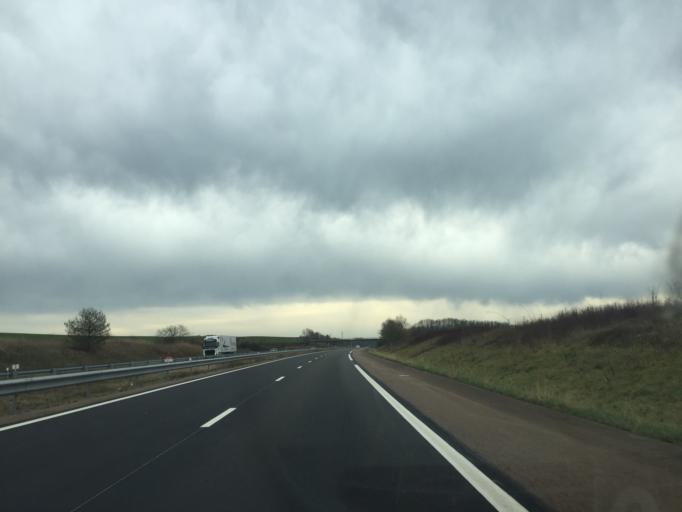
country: FR
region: Franche-Comte
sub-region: Departement du Jura
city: Bletterans
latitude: 46.7402
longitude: 5.5108
